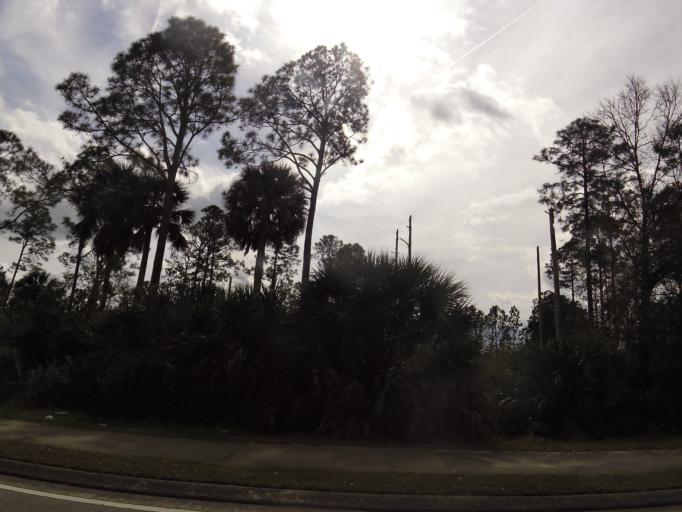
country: US
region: Florida
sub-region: Flagler County
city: Palm Coast
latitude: 29.5498
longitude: -81.2315
